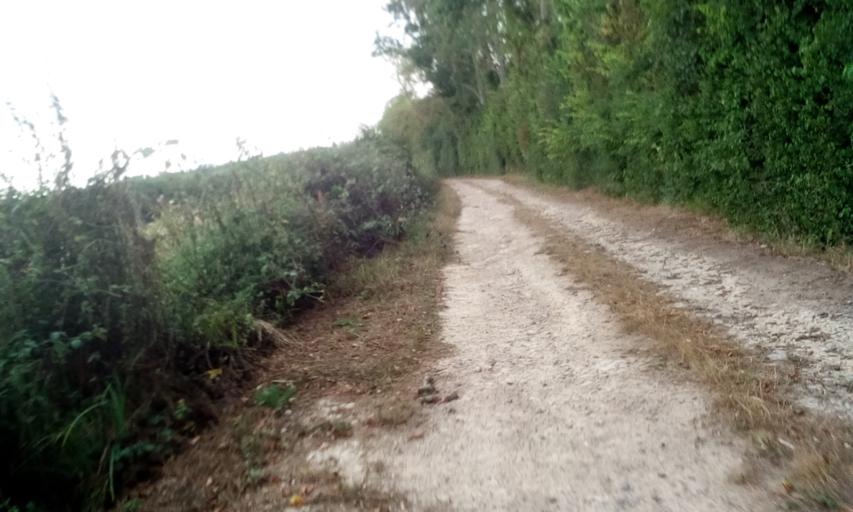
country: FR
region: Lower Normandy
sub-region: Departement du Calvados
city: Troarn
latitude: 49.1849
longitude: -0.2021
